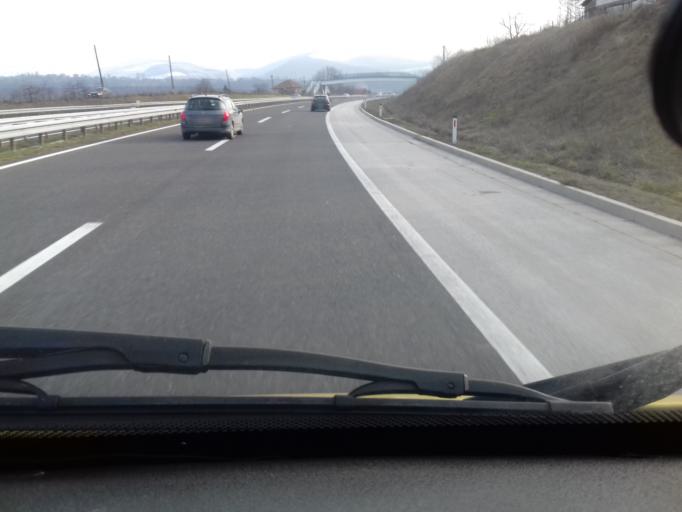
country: BA
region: Federation of Bosnia and Herzegovina
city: Kakanj
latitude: 44.1156
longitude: 18.1095
